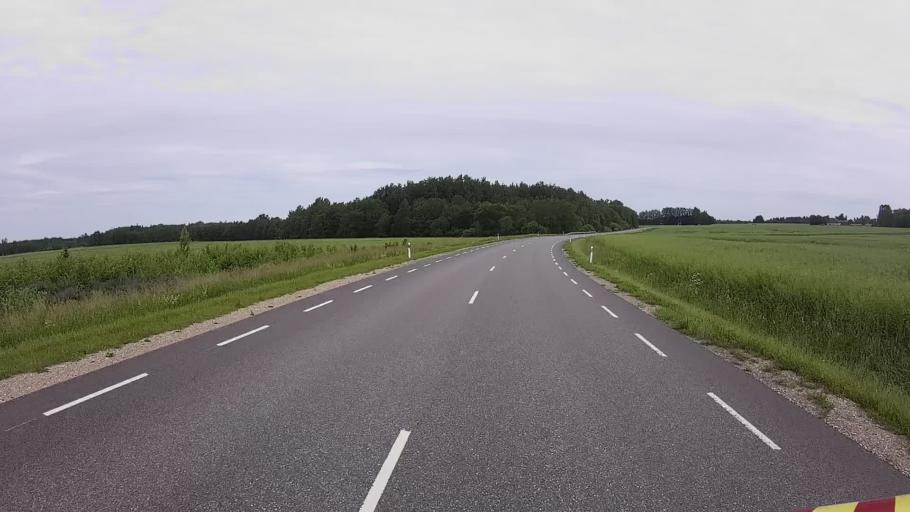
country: EE
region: Viljandimaa
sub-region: Karksi vald
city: Karksi-Nuia
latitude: 58.1695
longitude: 25.5803
